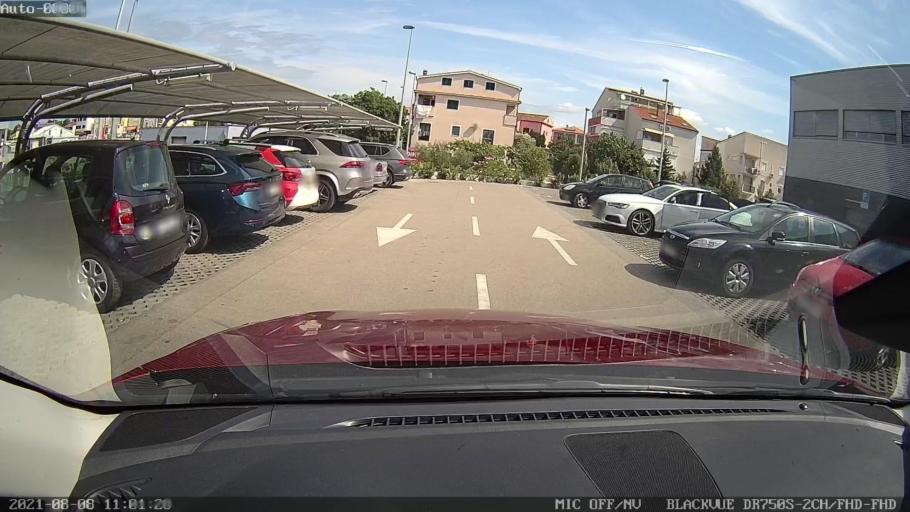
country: HR
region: Istarska
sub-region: Grad Rovinj
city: Rovinj
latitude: 45.0801
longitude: 13.6559
